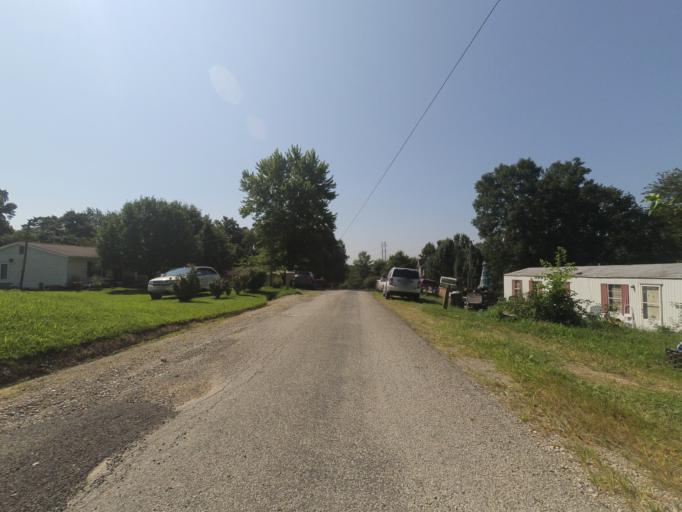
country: US
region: West Virginia
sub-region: Cabell County
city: Huntington
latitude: 38.4319
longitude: -82.4474
